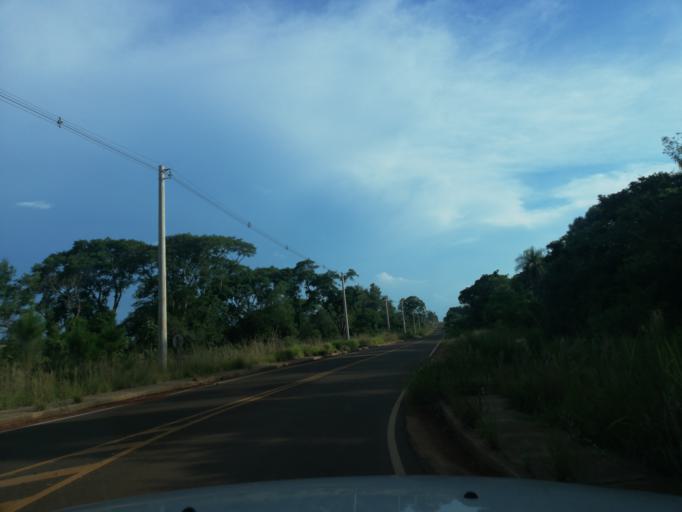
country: AR
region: Misiones
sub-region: Departamento de Candelaria
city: Candelaria
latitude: -27.4515
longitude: -55.7752
